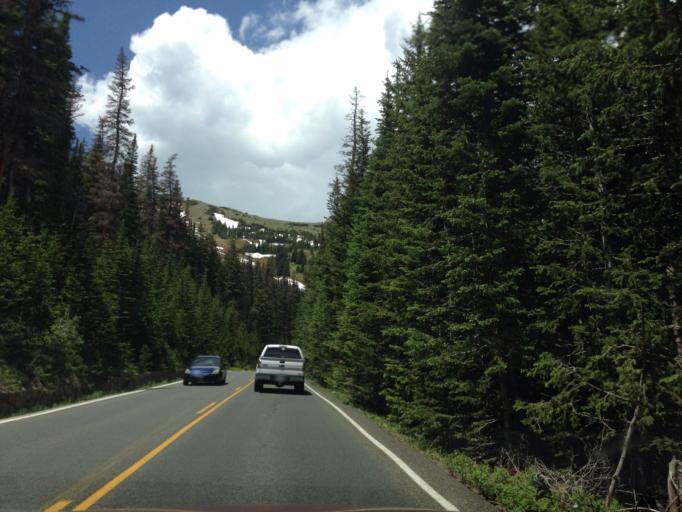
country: US
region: Colorado
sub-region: Larimer County
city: Estes Park
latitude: 40.3881
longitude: -105.6722
